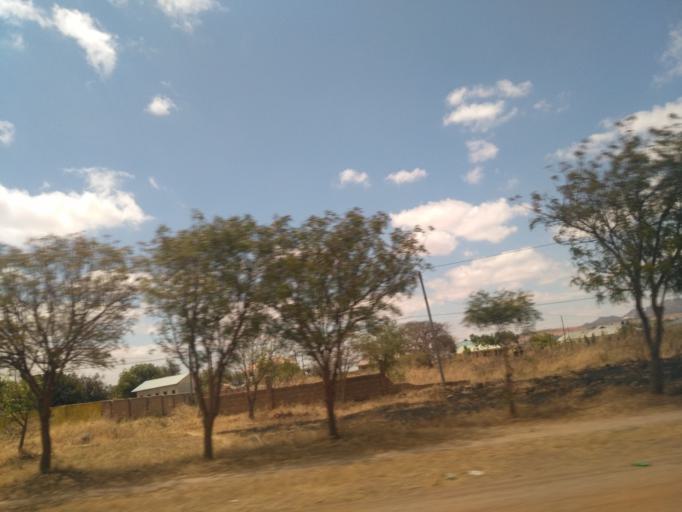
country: TZ
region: Dodoma
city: Kisasa
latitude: -6.1631
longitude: 35.7892
